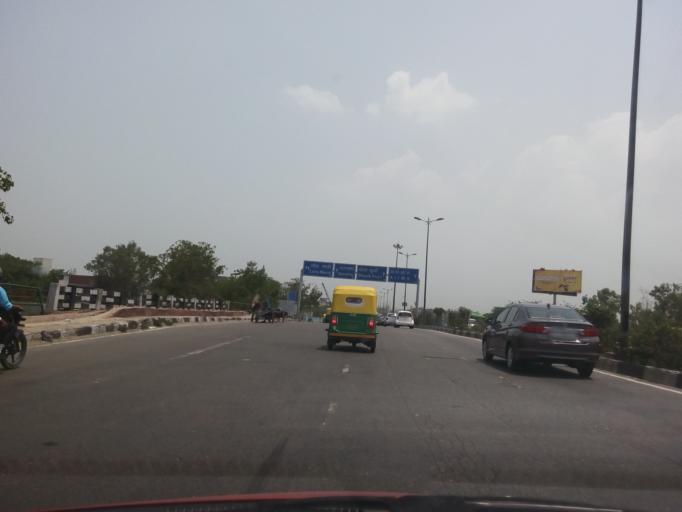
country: IN
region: NCT
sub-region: North West Delhi
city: Pitampura
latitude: 28.6320
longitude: 77.1322
